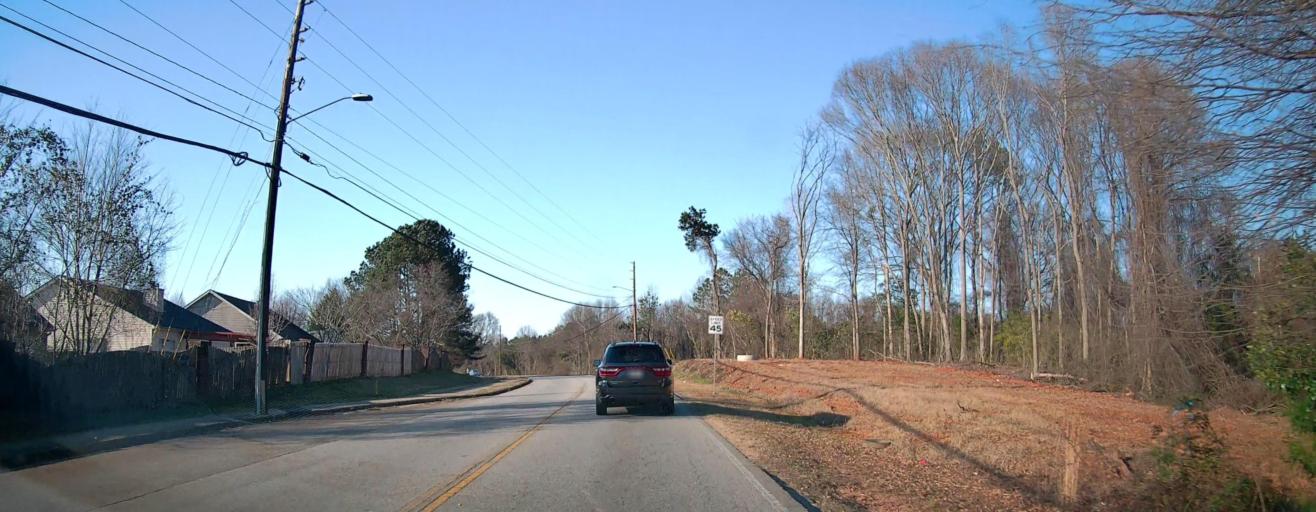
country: US
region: Georgia
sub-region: Clayton County
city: Lovejoy
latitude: 33.4437
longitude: -84.3158
